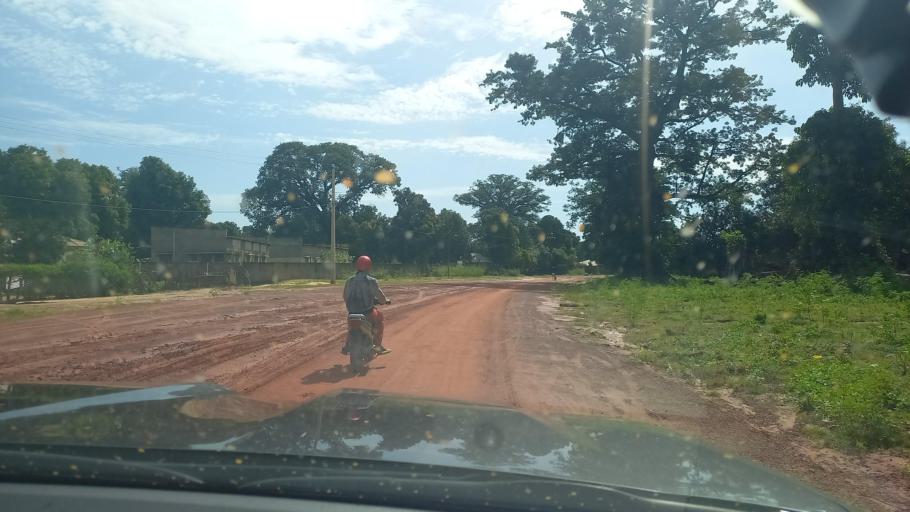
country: SN
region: Ziguinchor
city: Ziguinchor
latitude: 12.6758
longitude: -16.1972
